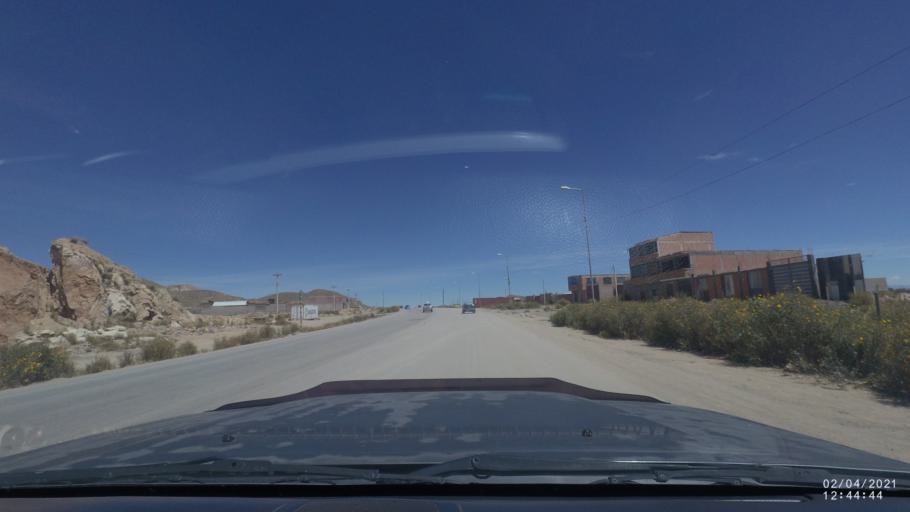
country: BO
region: Oruro
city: Oruro
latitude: -17.9293
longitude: -67.1297
